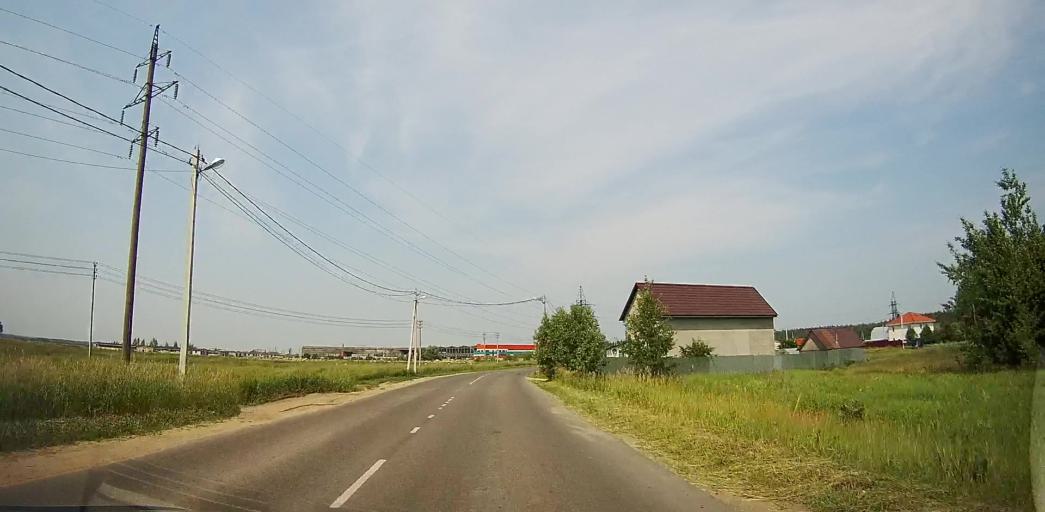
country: RU
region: Moskovskaya
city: Malyshevo
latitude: 55.5026
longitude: 38.3246
